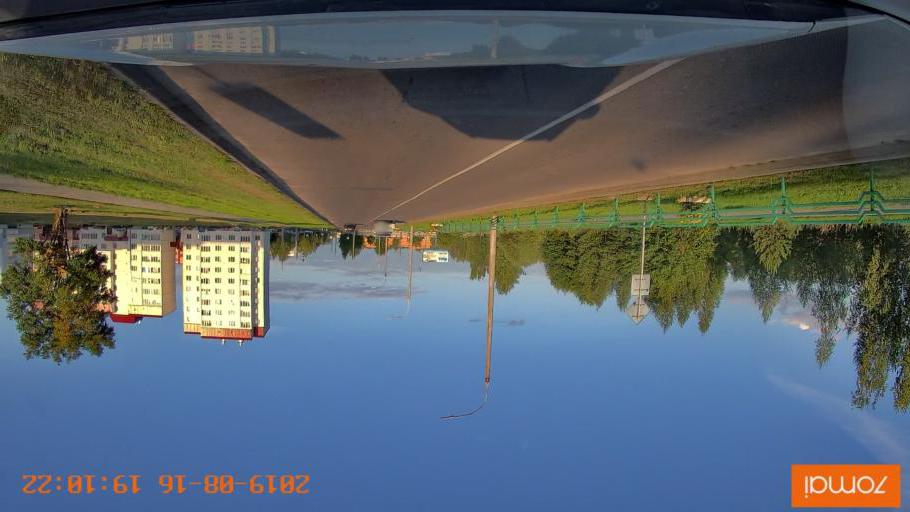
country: BY
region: Mogilev
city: Asipovichy
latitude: 53.3242
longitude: 28.6400
